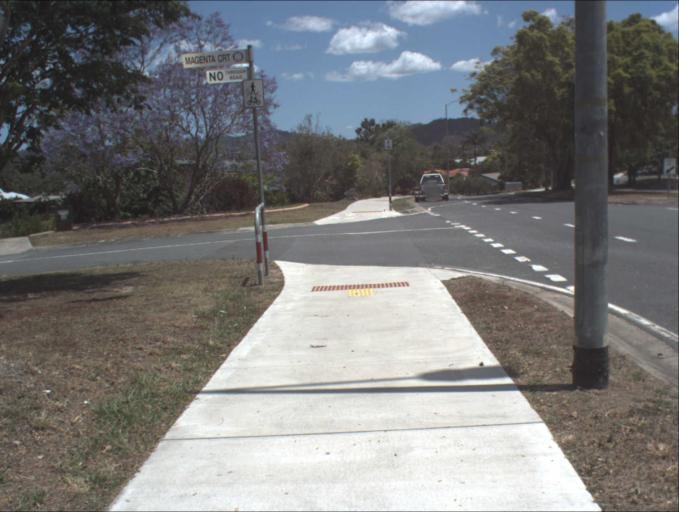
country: AU
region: Queensland
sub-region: Logan
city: Windaroo
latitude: -27.7360
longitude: 153.2057
